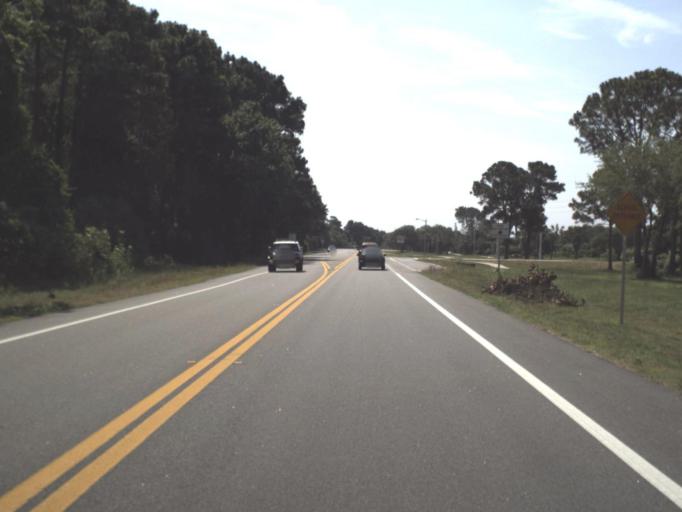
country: US
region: Florida
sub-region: Saint Johns County
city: Palm Valley
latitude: 30.1697
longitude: -81.3707
